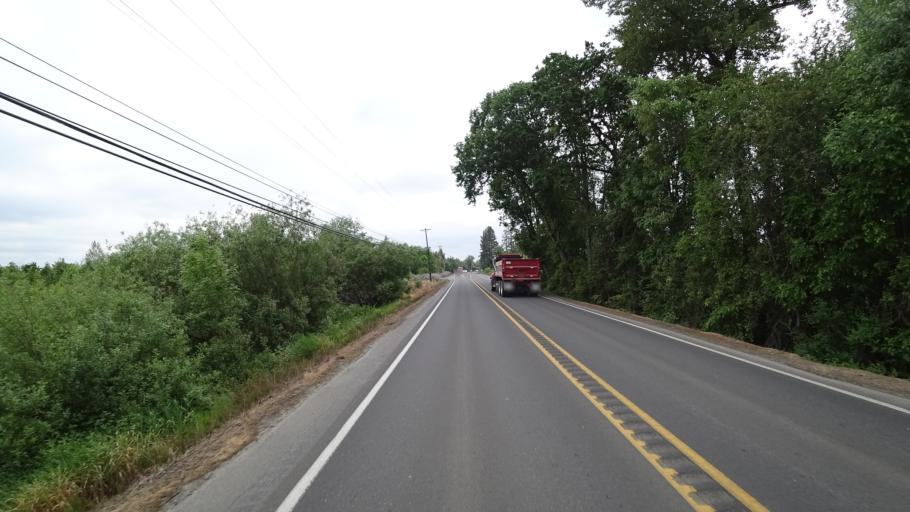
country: US
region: Oregon
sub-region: Washington County
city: Hillsboro
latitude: 45.5037
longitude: -122.9909
